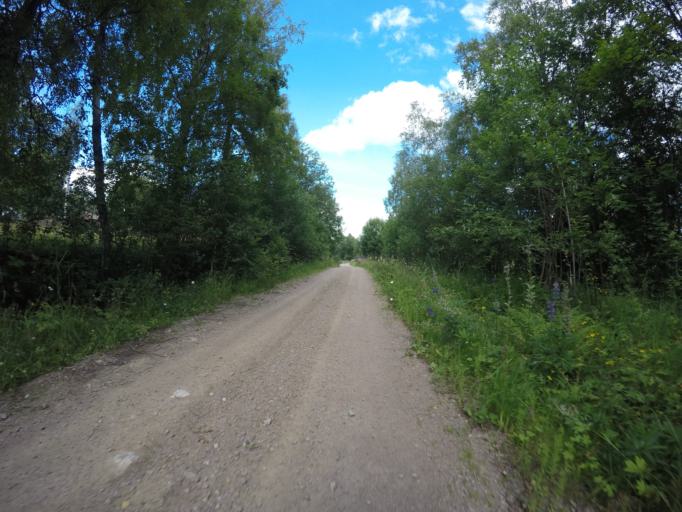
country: SE
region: OErebro
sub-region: Hallefors Kommun
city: Haellefors
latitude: 60.0685
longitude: 14.4631
